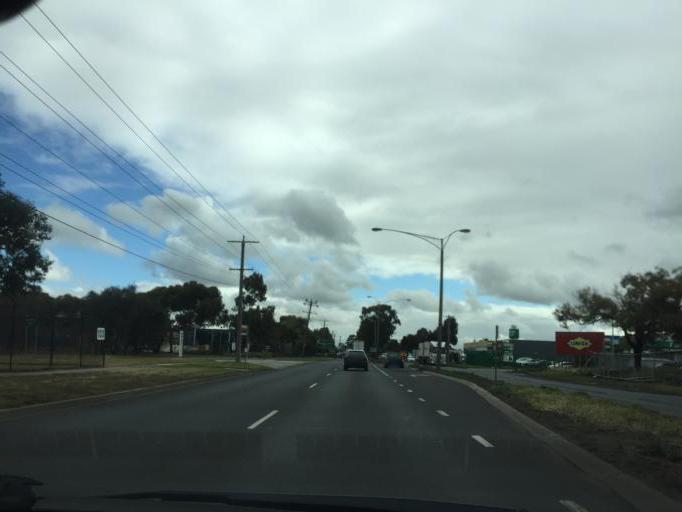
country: AU
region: Victoria
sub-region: Brimbank
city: Sunshine West
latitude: -37.8082
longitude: 144.8184
